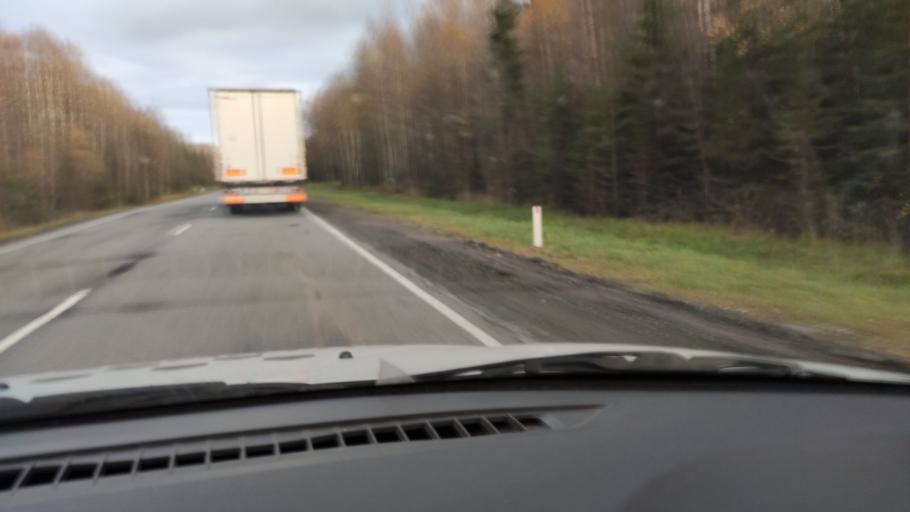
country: RU
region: Kirov
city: Chernaya Kholunitsa
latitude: 58.7721
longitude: 51.9481
